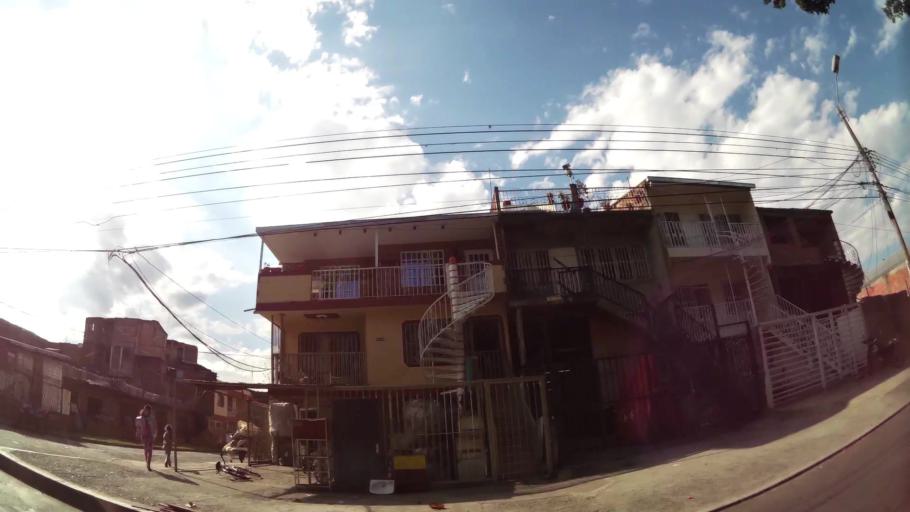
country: CO
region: Valle del Cauca
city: Cali
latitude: 3.4077
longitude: -76.5049
